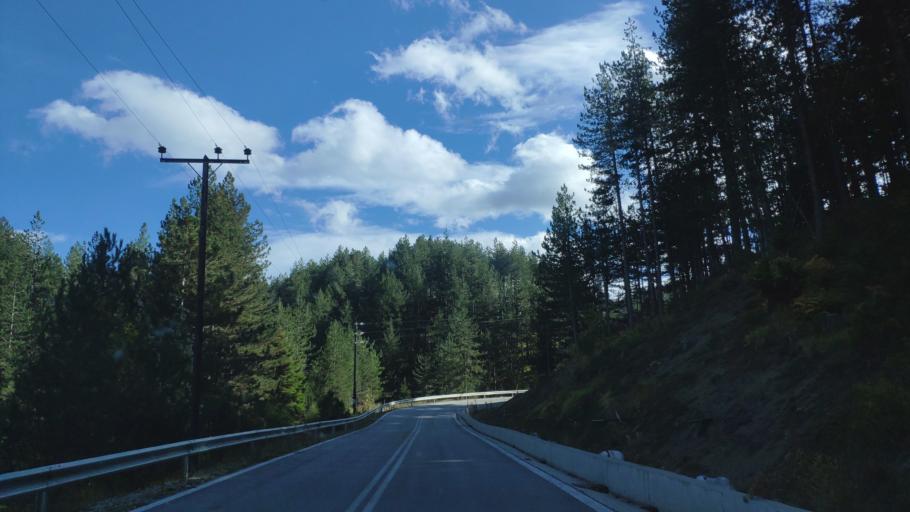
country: AL
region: Korce
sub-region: Rrethi i Devollit
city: Miras
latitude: 40.4085
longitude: 20.8774
